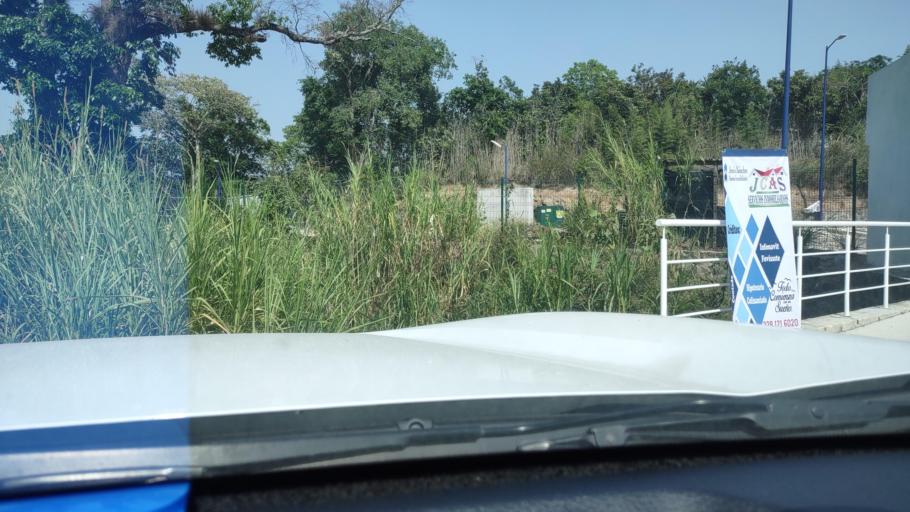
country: MX
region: Veracruz
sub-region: Emiliano Zapata
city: Jacarandas
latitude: 19.5128
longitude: -96.8477
